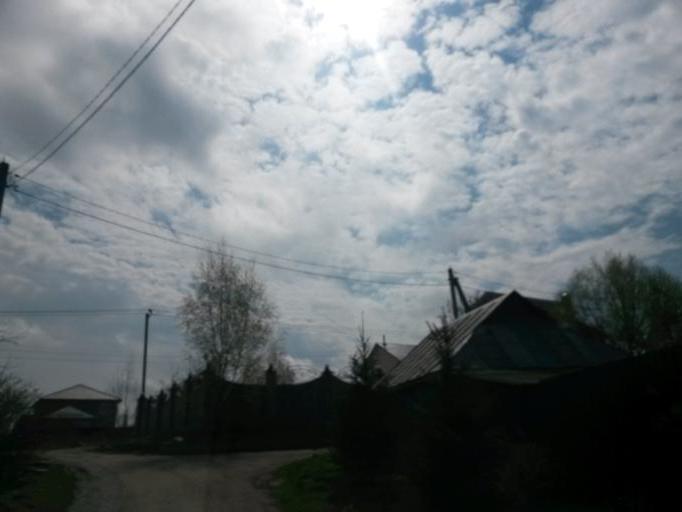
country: RU
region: Moskovskaya
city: Lyubuchany
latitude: 55.2557
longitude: 37.6044
